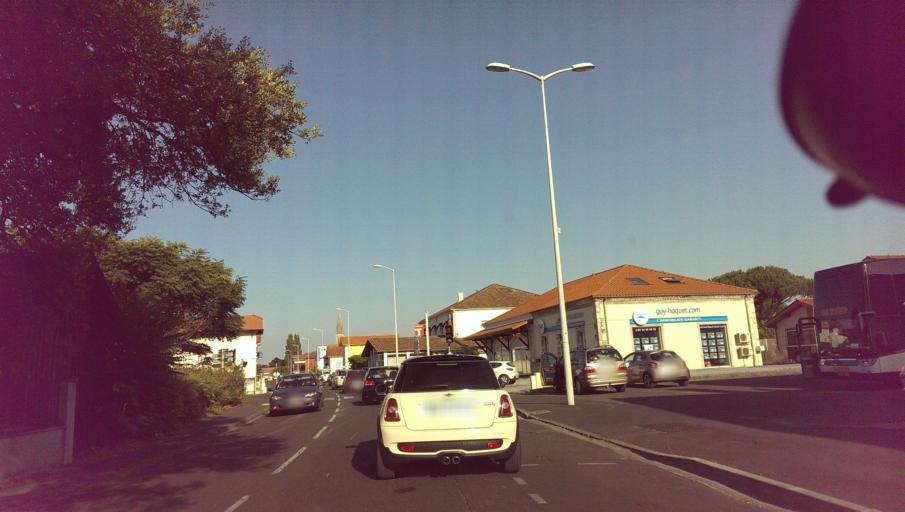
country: FR
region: Aquitaine
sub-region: Departement des Landes
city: Mimizan
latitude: 44.2030
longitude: -1.2339
